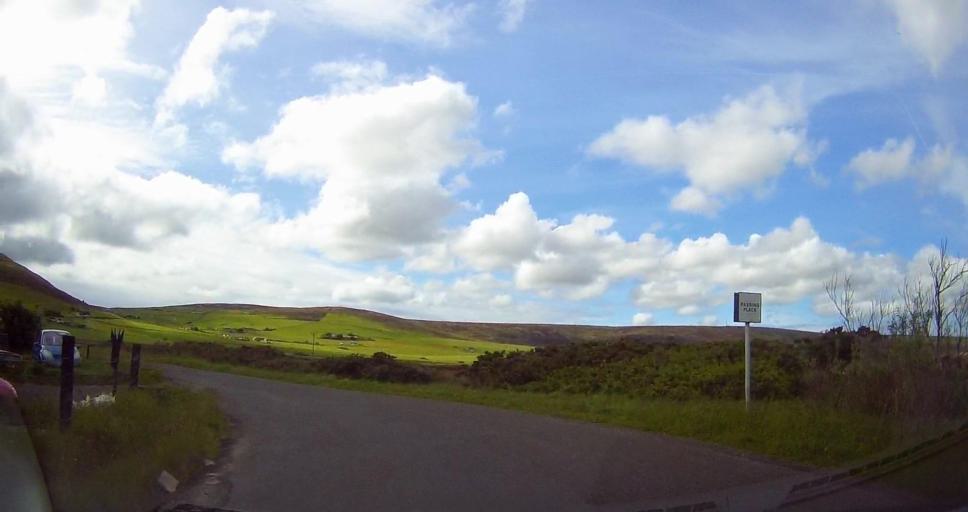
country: GB
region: Scotland
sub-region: Orkney Islands
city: Orkney
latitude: 59.0481
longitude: -3.0846
